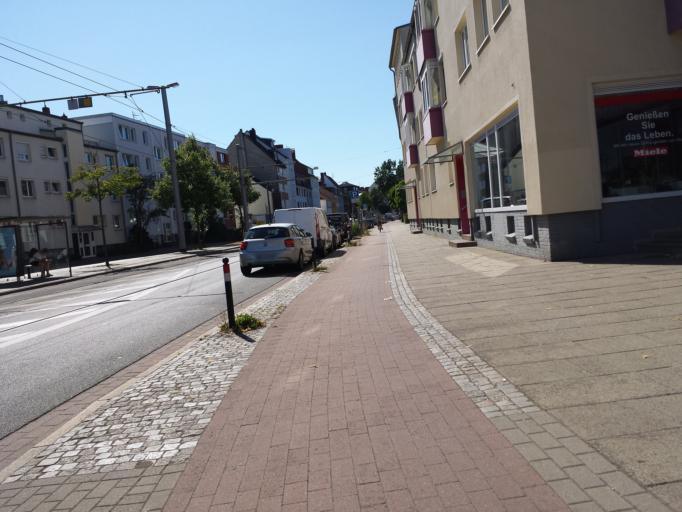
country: DE
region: Bremen
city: Bremen
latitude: 53.0706
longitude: 8.8559
